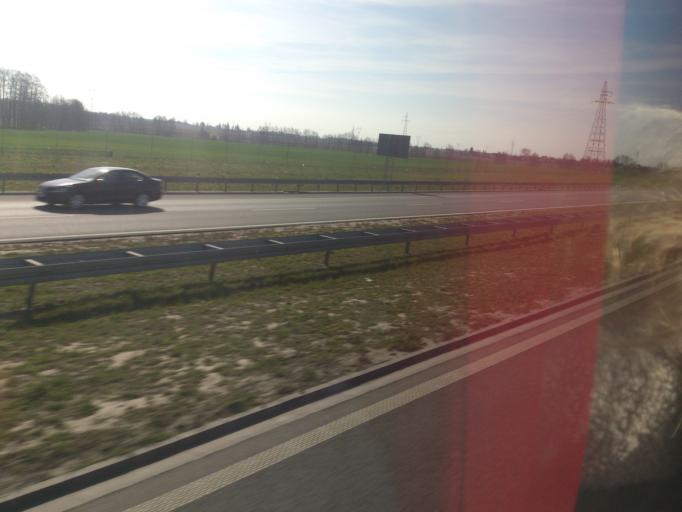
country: PL
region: Kujawsko-Pomorskie
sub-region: Powiat wloclawski
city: Lubanie
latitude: 52.7393
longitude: 18.8584
